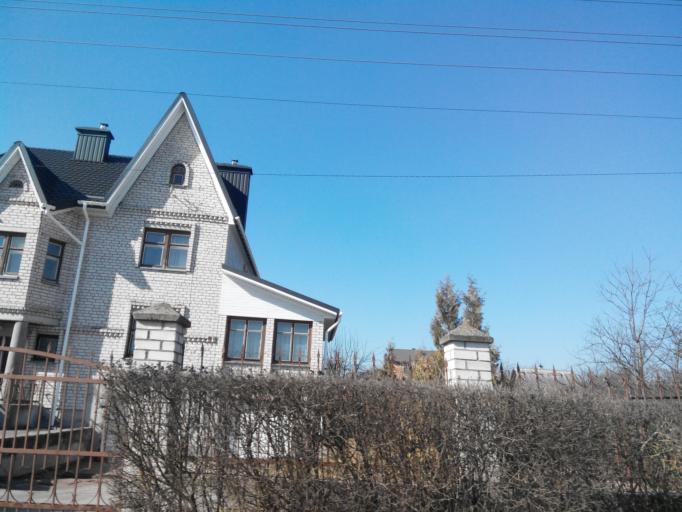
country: BY
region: Minsk
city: Zhdanovichy
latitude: 53.9180
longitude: 27.3971
